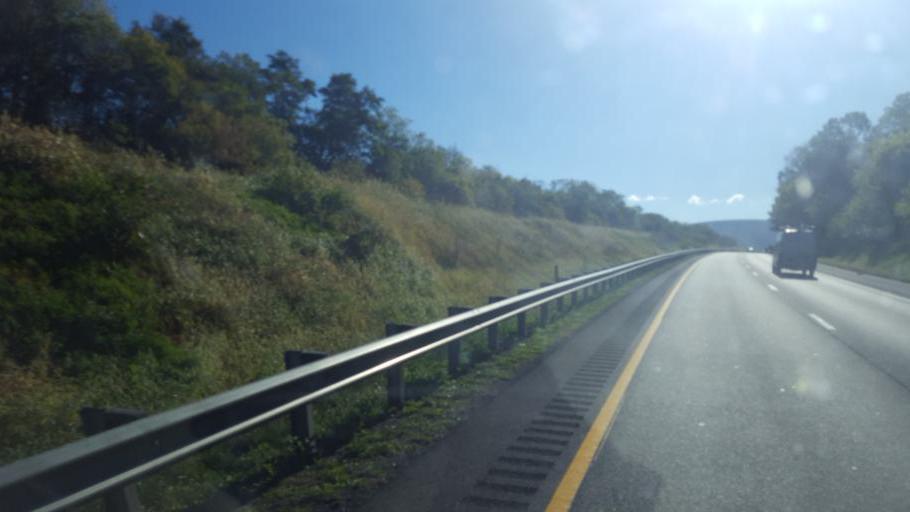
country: US
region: Maryland
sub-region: Washington County
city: Robinwood
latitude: 39.5991
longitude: -77.6635
